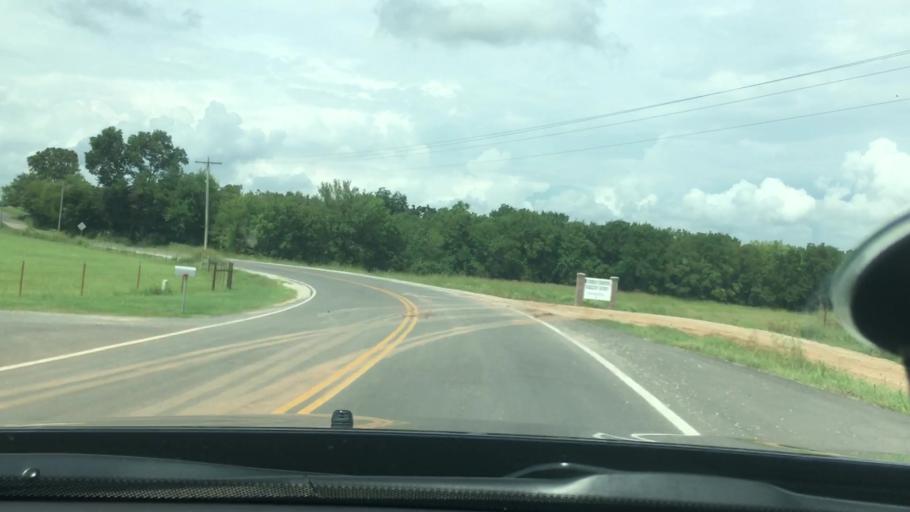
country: US
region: Oklahoma
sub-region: Carter County
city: Dickson
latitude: 34.2305
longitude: -96.9100
